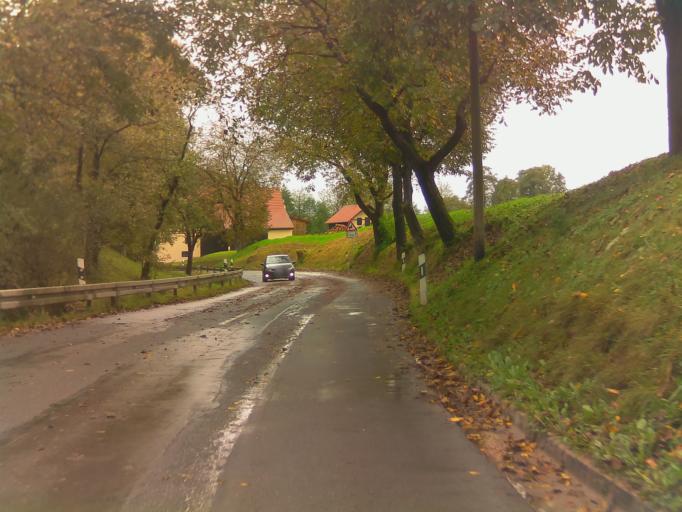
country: DE
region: Bavaria
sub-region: Upper Franconia
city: Wattendorf
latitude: 50.0198
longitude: 11.0875
